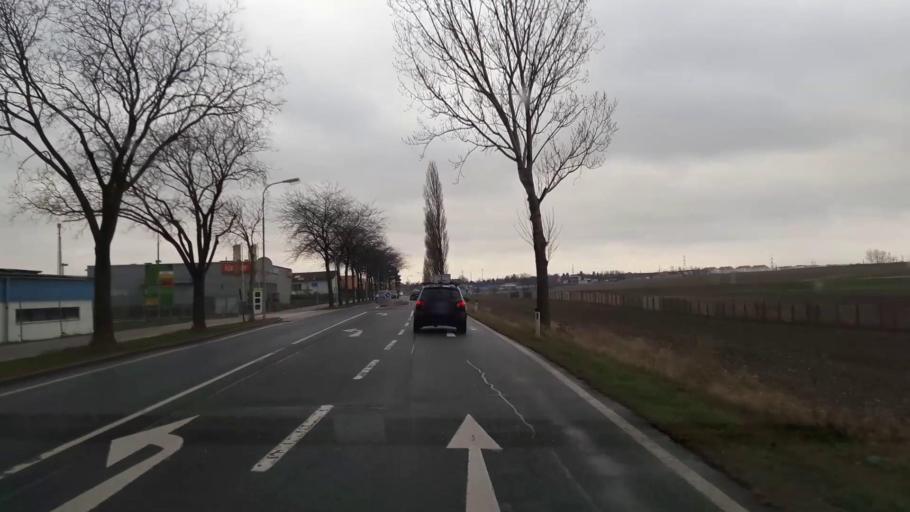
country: AT
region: Lower Austria
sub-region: Politischer Bezirk Wien-Umgebung
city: Zwolfaxing
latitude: 48.1194
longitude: 16.4556
